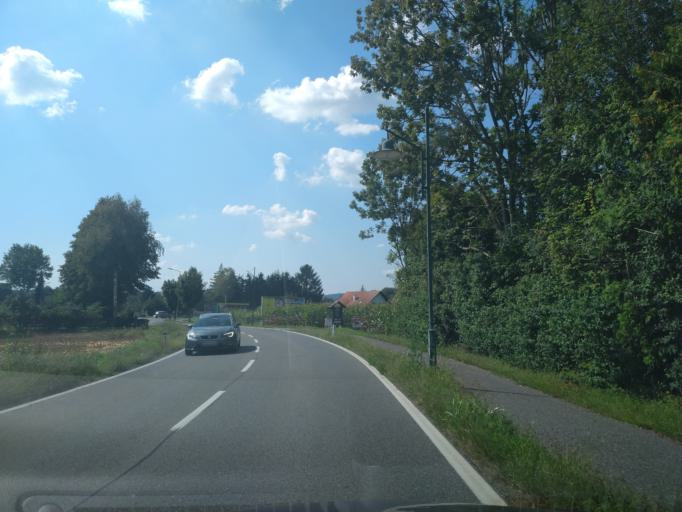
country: AT
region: Styria
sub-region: Politischer Bezirk Leibnitz
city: Gabersdorf
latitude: 46.7640
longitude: 15.5820
